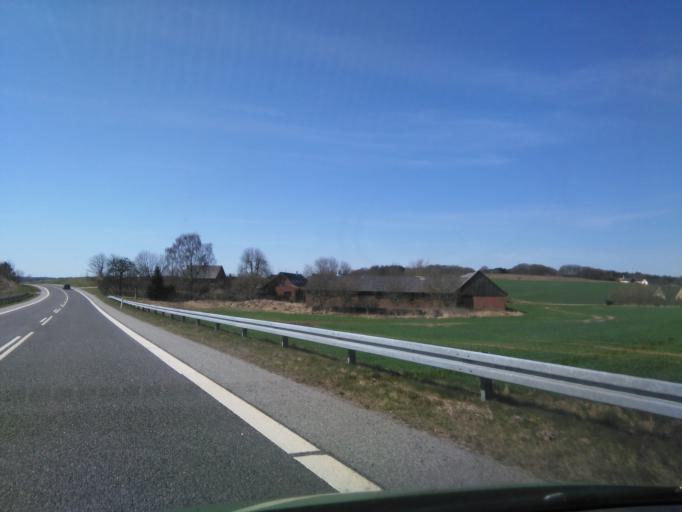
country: DK
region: Central Jutland
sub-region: Skanderborg Kommune
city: Ry
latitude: 56.0219
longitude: 9.7231
